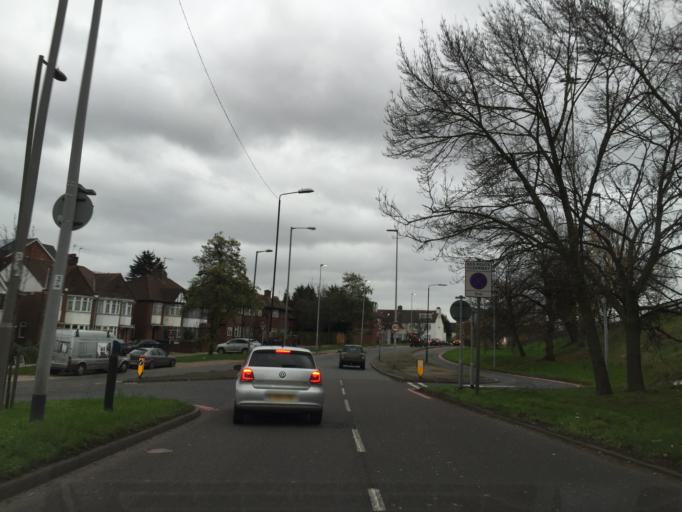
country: GB
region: England
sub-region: Greater London
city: Hendon
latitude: 51.5765
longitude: -0.2169
